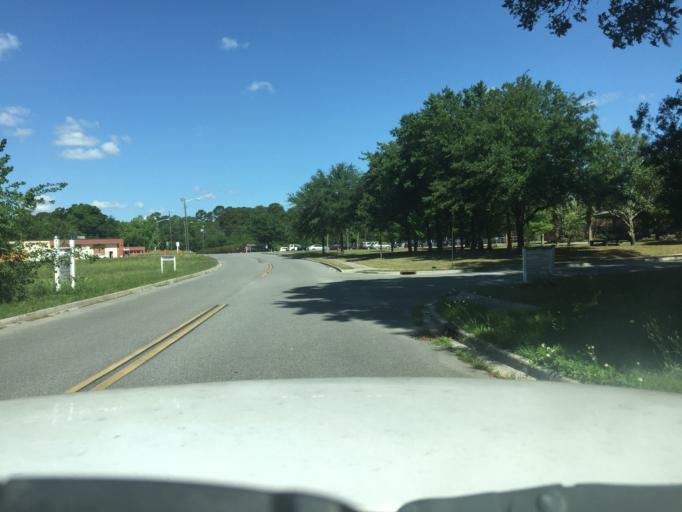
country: US
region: Georgia
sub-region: Chatham County
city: Isle of Hope
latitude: 32.0040
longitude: -81.0989
